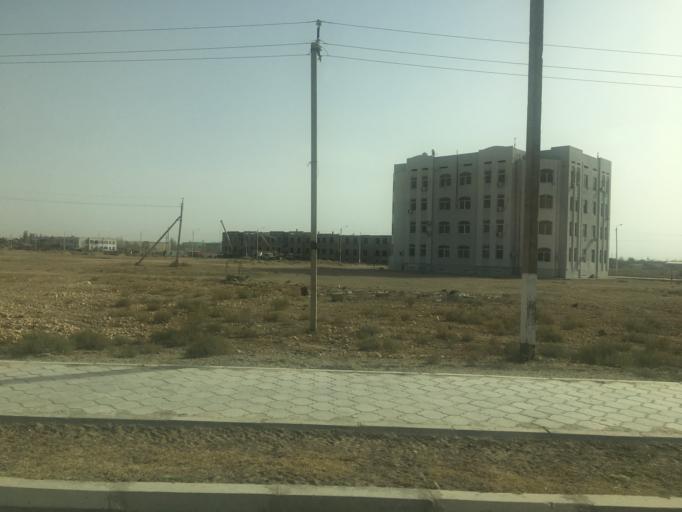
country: TM
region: Lebap
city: Gazojak
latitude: 41.1795
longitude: 61.4023
